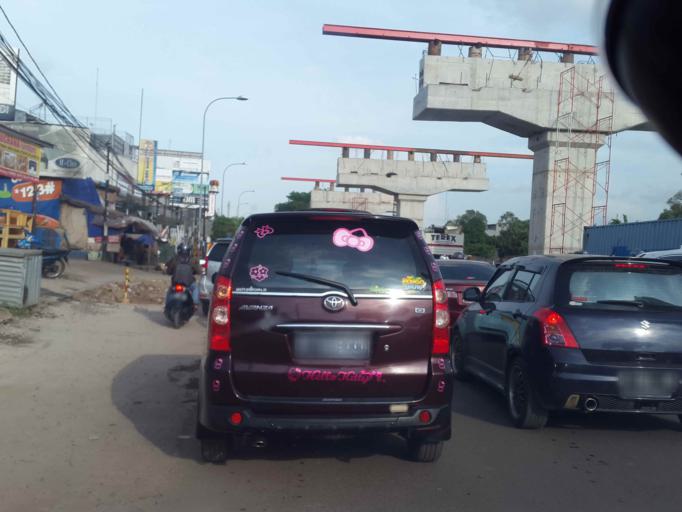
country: ID
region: West Java
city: Bekasi
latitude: -6.2497
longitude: 106.9473
